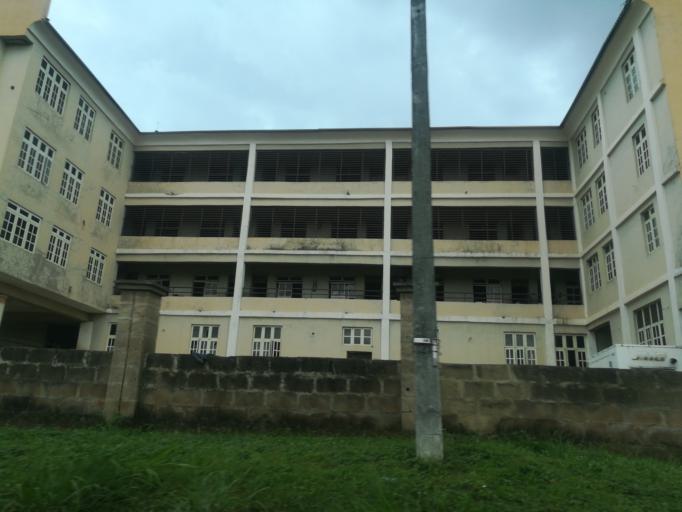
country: NG
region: Oyo
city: Ibadan
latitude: 7.4316
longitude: 3.8973
